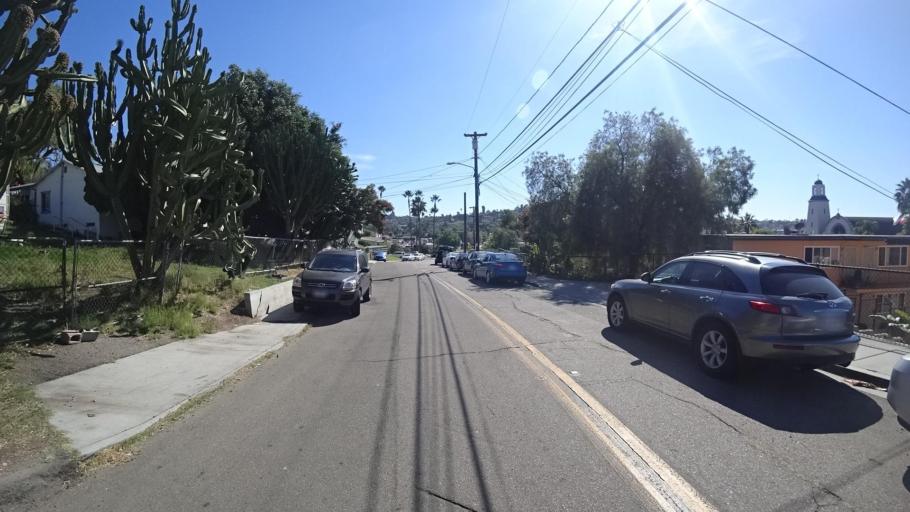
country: US
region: California
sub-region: San Diego County
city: Spring Valley
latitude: 32.7500
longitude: -116.9835
